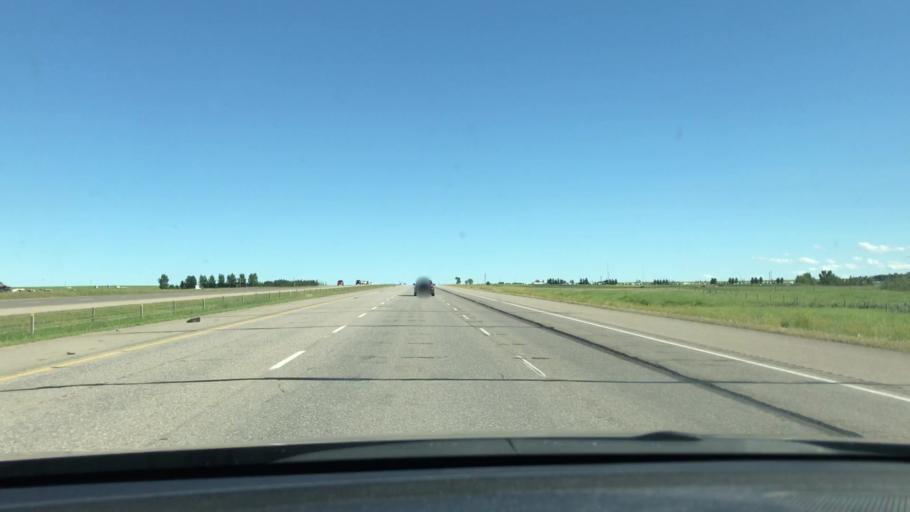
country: CA
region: Alberta
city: Crossfield
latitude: 51.4583
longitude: -114.0216
